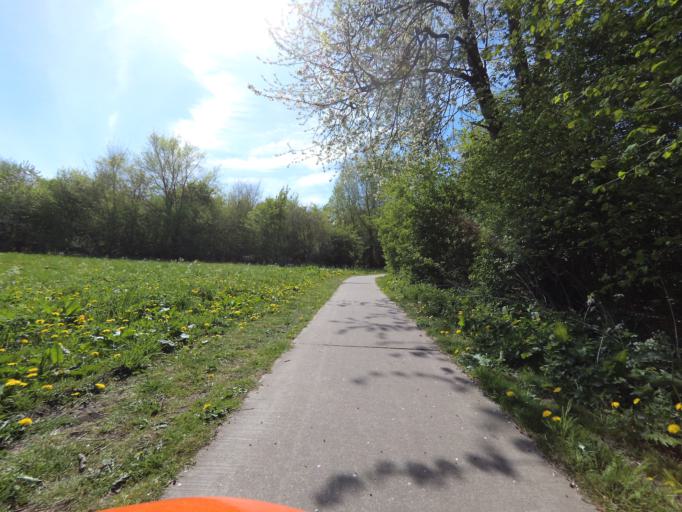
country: NL
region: Flevoland
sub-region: Gemeente Dronten
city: Dronten
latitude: 52.5254
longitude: 5.6925
